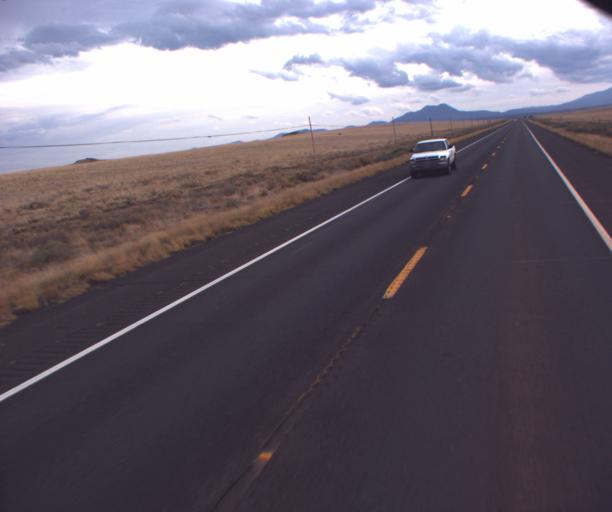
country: US
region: Arizona
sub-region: Coconino County
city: Flagstaff
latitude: 35.6176
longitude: -111.5226
